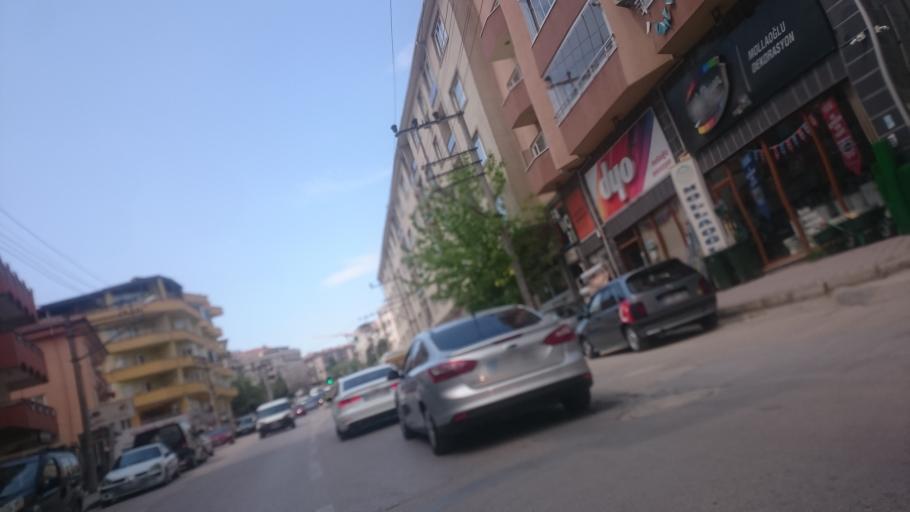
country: TR
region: Bursa
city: Yildirim
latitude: 40.2220
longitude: 28.9879
